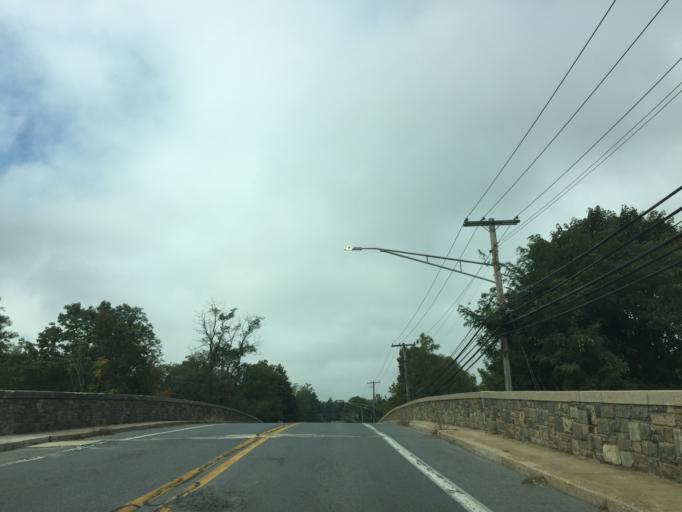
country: US
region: Maryland
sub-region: Baltimore County
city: Reisterstown
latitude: 39.4754
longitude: -76.8198
